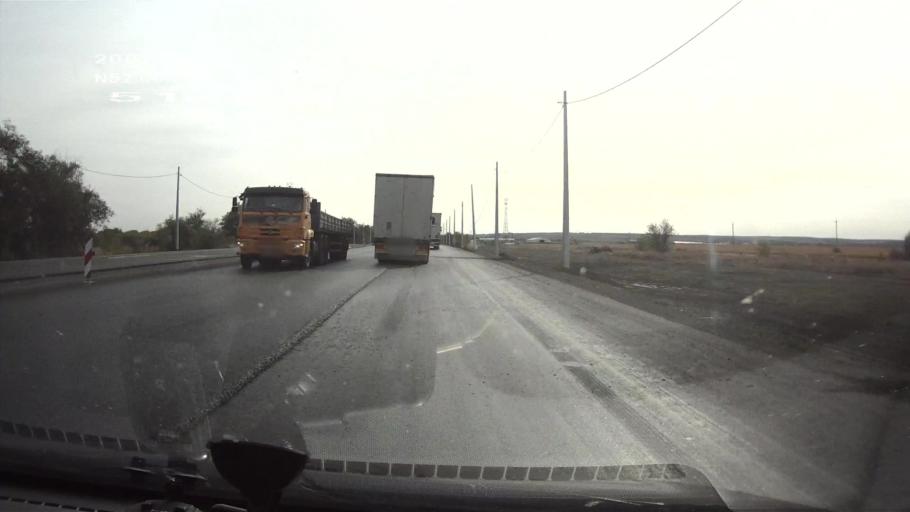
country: RU
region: Saratov
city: Sinodskoye
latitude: 52.0030
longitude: 46.6820
